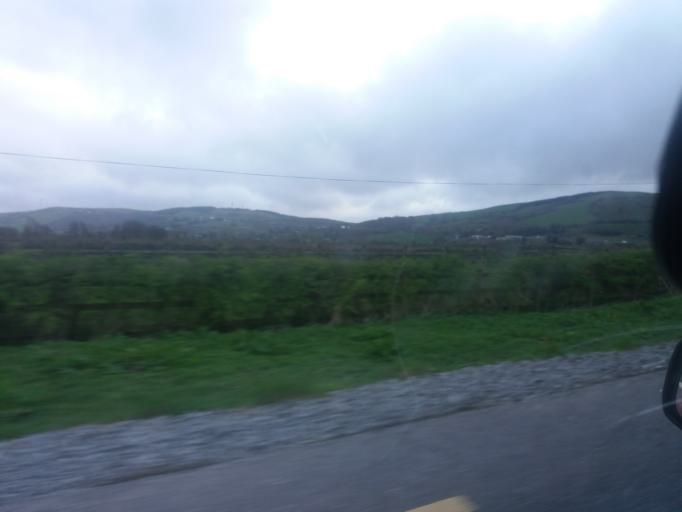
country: IE
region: Munster
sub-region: County Limerick
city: Newcastle West
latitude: 52.4352
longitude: -9.1185
